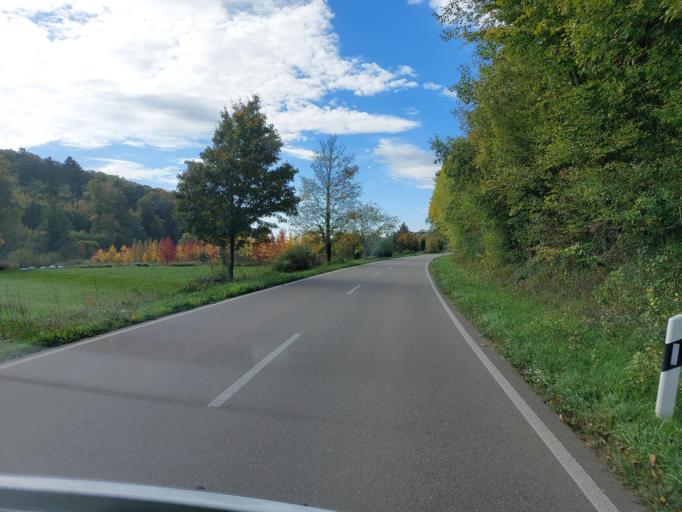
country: DE
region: Baden-Wuerttemberg
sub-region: Freiburg Region
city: Malterdingen
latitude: 48.1562
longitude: 7.8263
